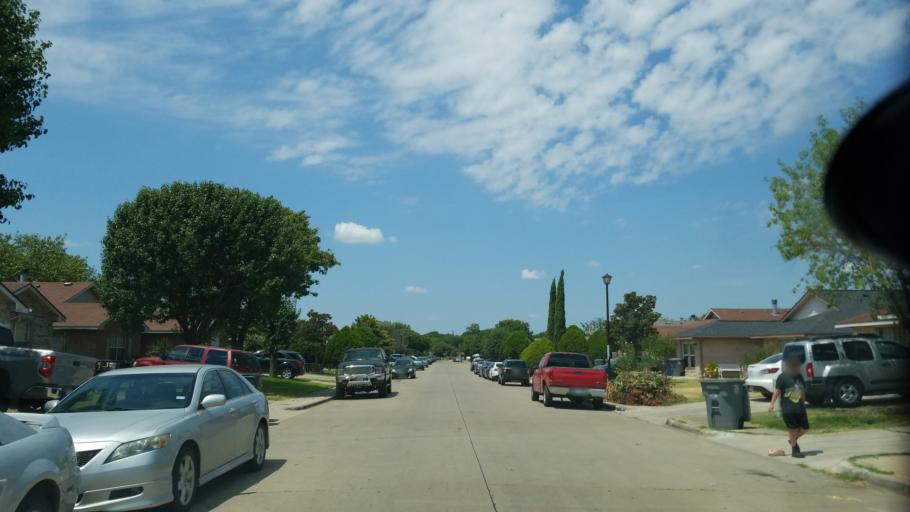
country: US
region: Texas
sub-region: Dallas County
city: Cockrell Hill
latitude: 32.7265
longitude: -96.8931
